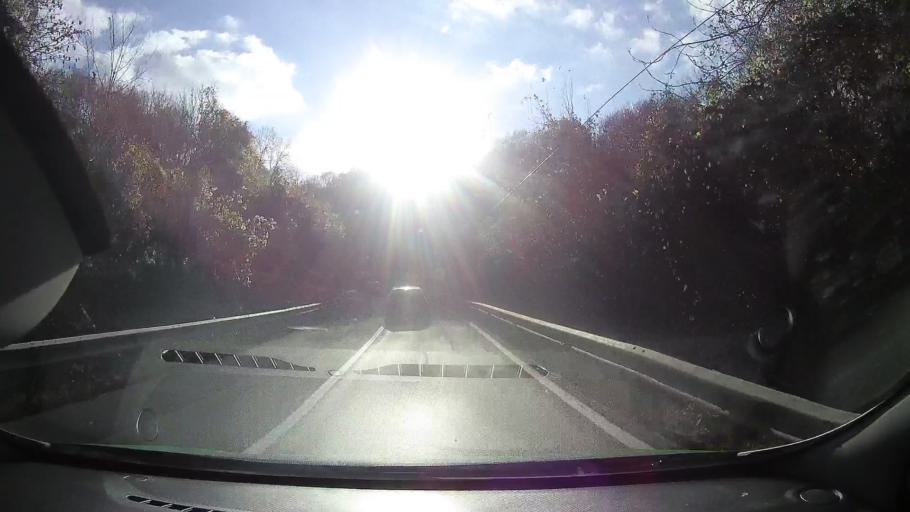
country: RO
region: Tulcea
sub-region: Comuna Topolog
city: Topolog
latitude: 44.9137
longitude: 28.4198
